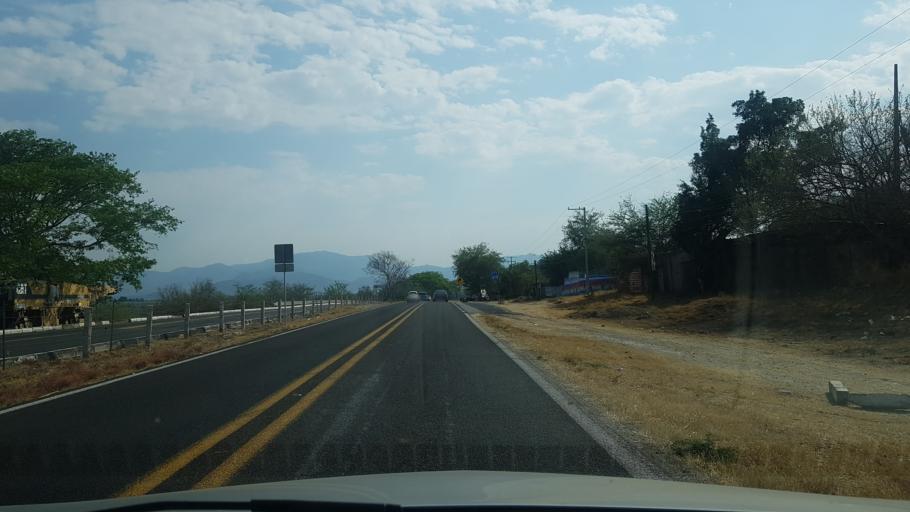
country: MX
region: Morelos
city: Puente de Ixtla
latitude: 18.6438
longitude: -99.3041
